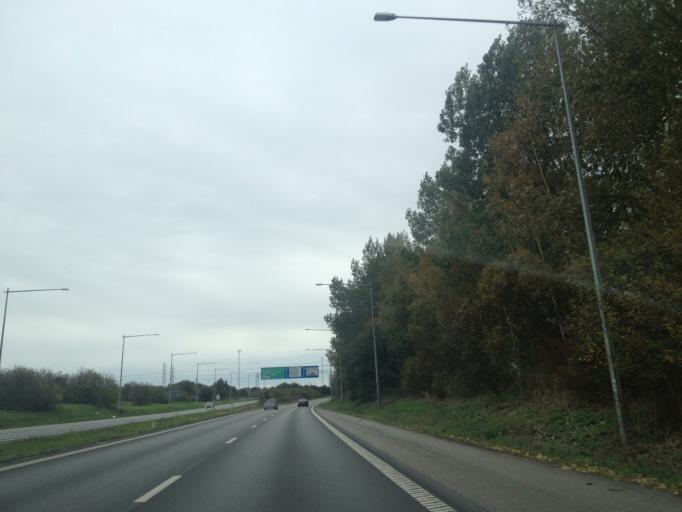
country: SE
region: Skane
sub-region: Burlovs Kommun
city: Arloev
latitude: 55.6312
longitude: 13.0549
